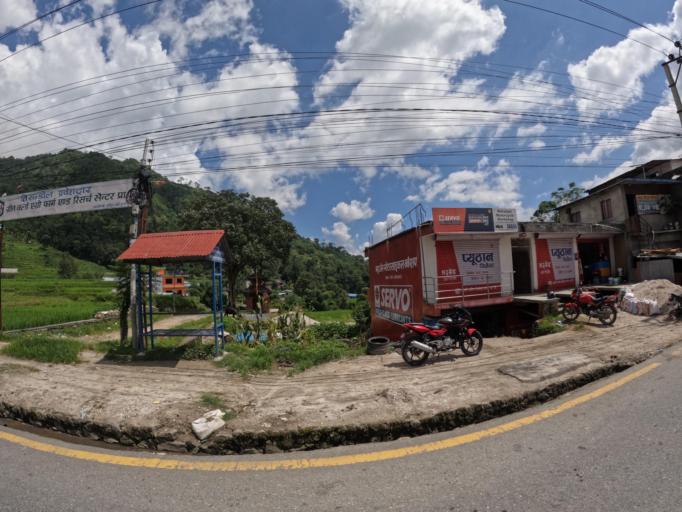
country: NP
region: Central Region
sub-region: Bagmati Zone
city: Kathmandu
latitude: 27.7860
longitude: 85.3281
